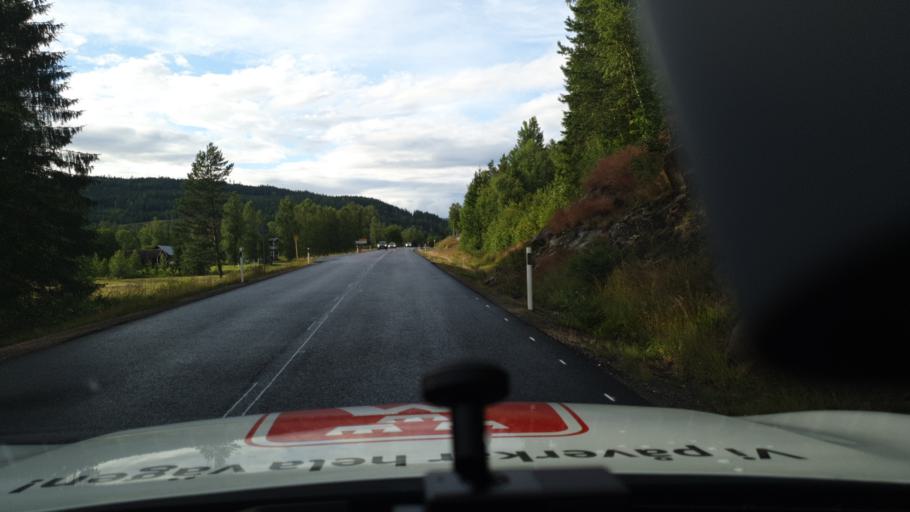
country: SE
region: Vaermland
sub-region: Torsby Kommun
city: Torsby
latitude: 60.2384
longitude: 13.0102
